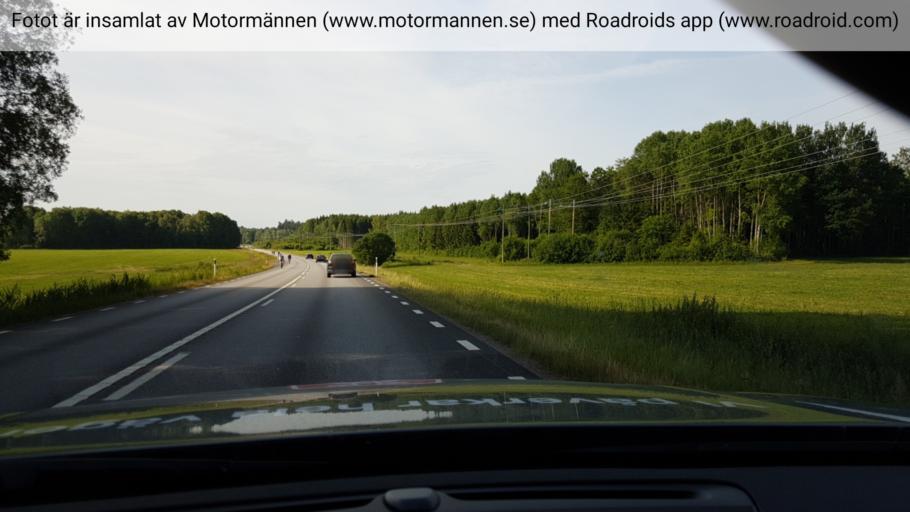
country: SE
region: OErebro
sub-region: Askersunds Kommun
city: Askersund
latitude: 58.7746
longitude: 14.7971
